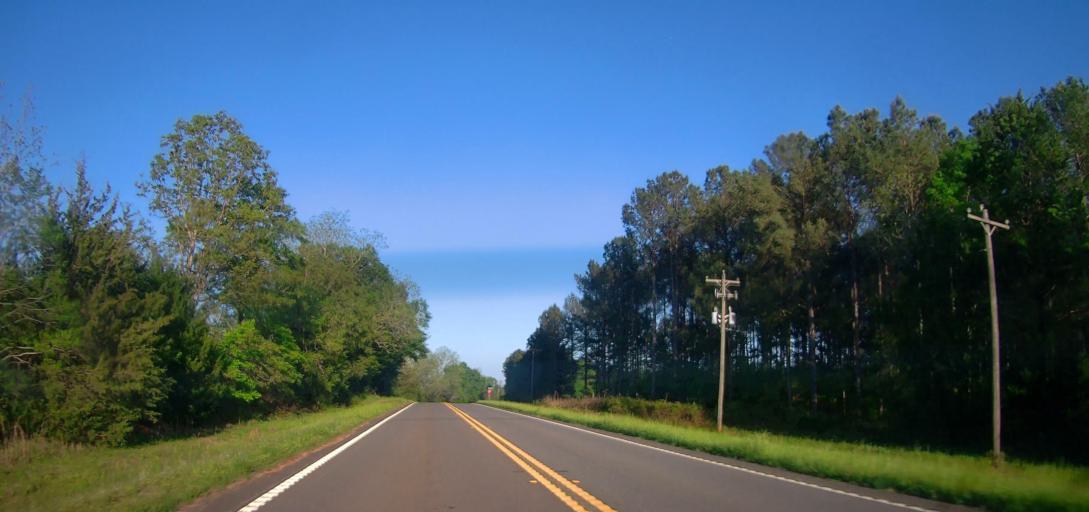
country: US
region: Georgia
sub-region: Schley County
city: Ellaville
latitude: 32.3199
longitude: -84.2635
